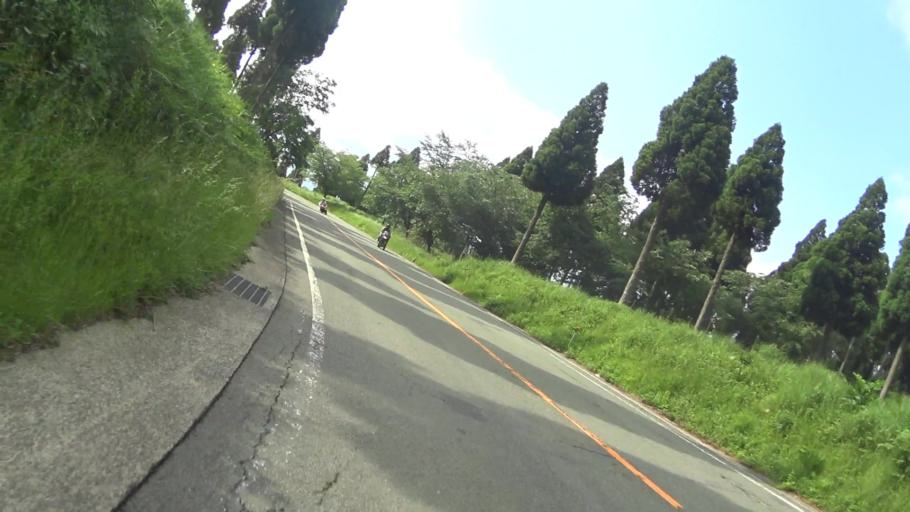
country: JP
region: Kumamoto
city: Aso
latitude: 32.8925
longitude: 131.0489
